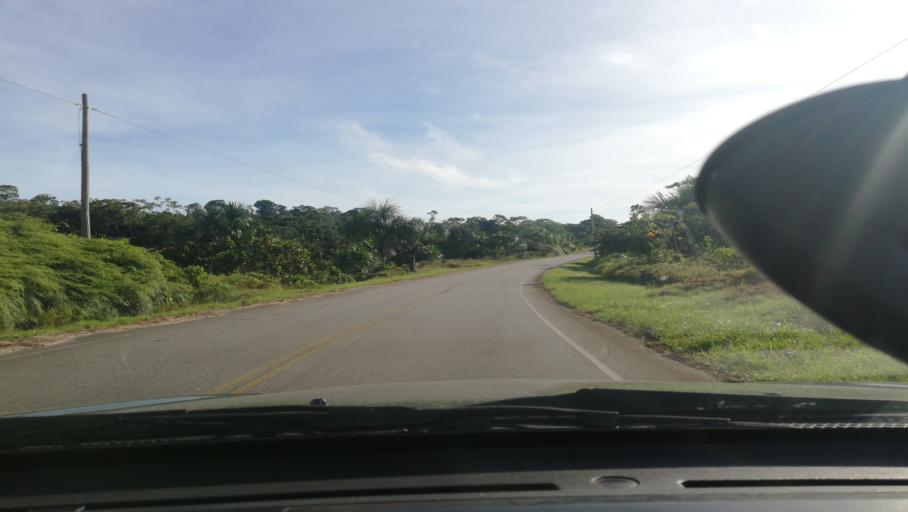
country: PE
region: Loreto
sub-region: Provincia de Loreto
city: Nauta
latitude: -4.3944
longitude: -73.5727
